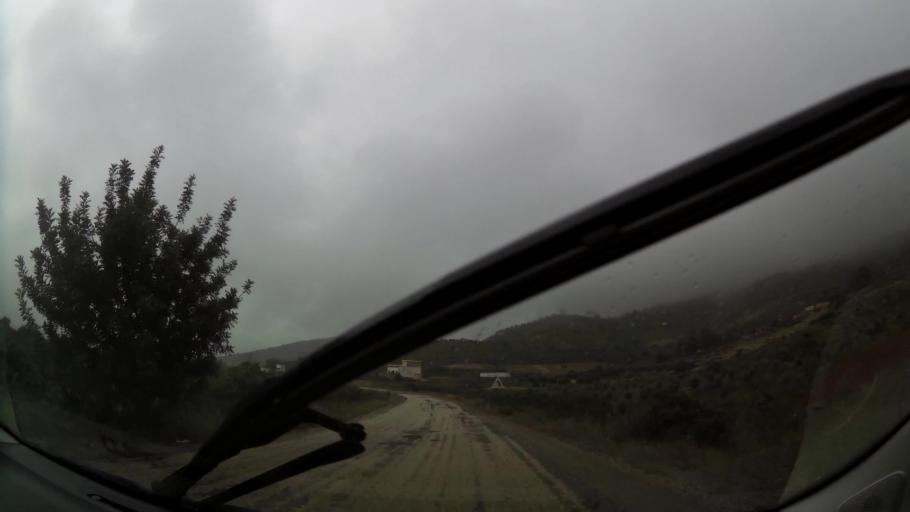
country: MA
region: Taza-Al Hoceima-Taounate
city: Imzourene
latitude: 35.1219
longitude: -3.7786
